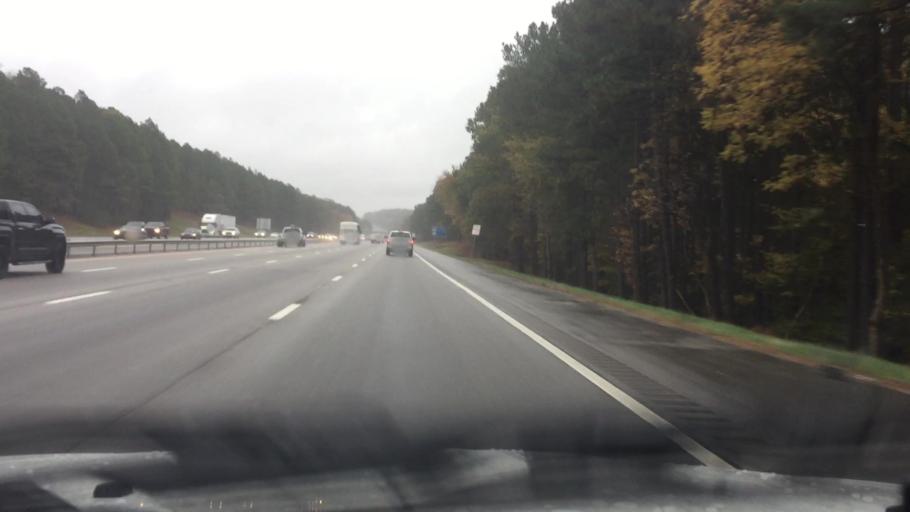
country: US
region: North Carolina
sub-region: Wake County
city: Morrisville
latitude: 35.8452
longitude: -78.7911
